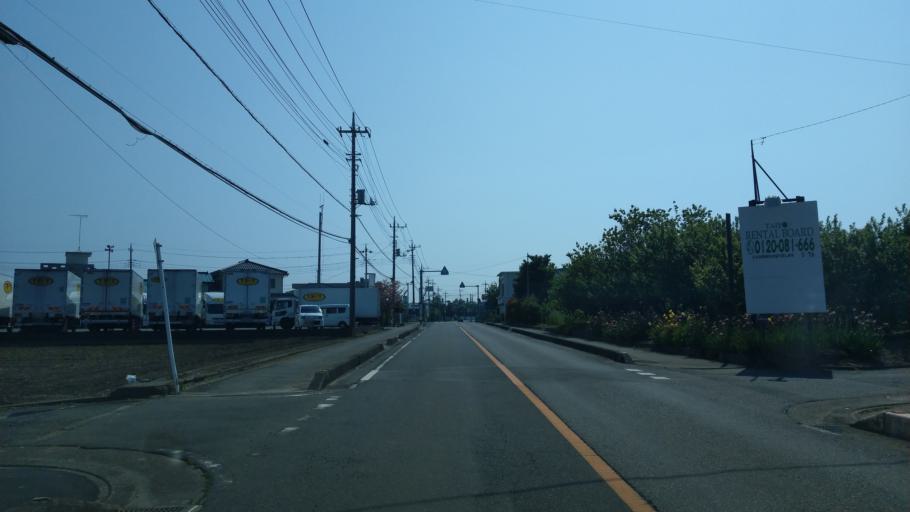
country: JP
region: Saitama
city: Kamifukuoka
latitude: 35.8799
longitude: 139.5456
